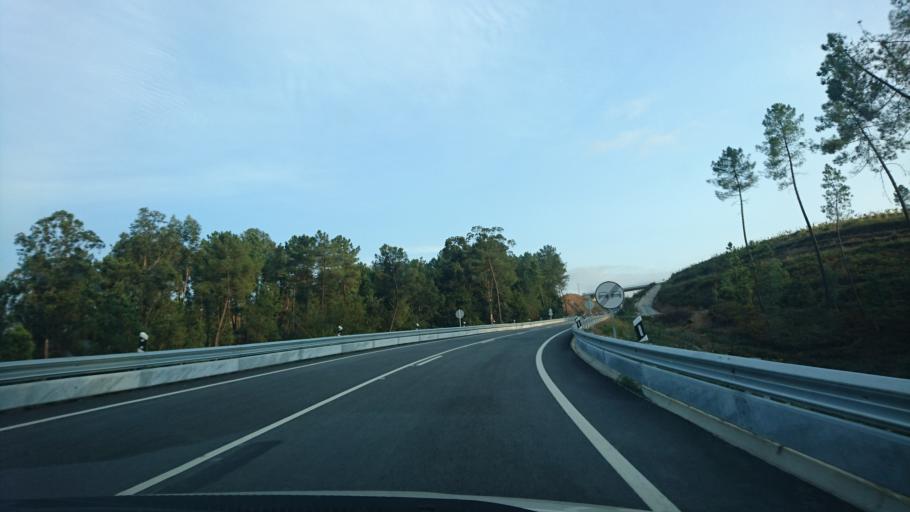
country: PT
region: Vila Real
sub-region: Mondim de Basto
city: Mondim de Basto
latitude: 41.4070
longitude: -7.9817
